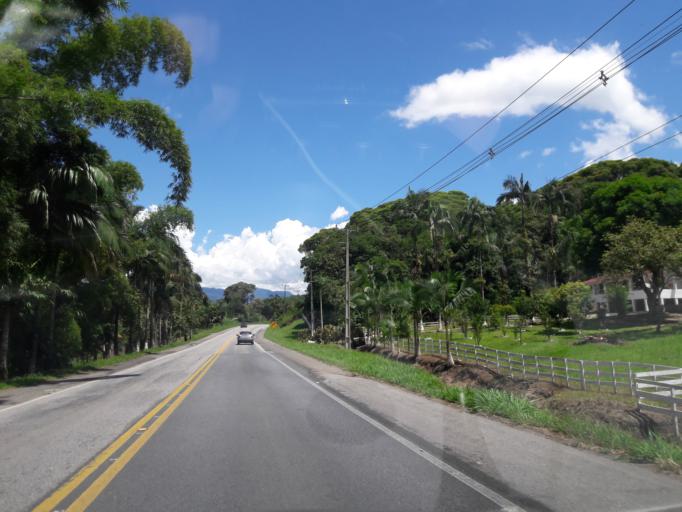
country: BR
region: Parana
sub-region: Antonina
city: Antonina
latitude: -25.4534
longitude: -48.8070
